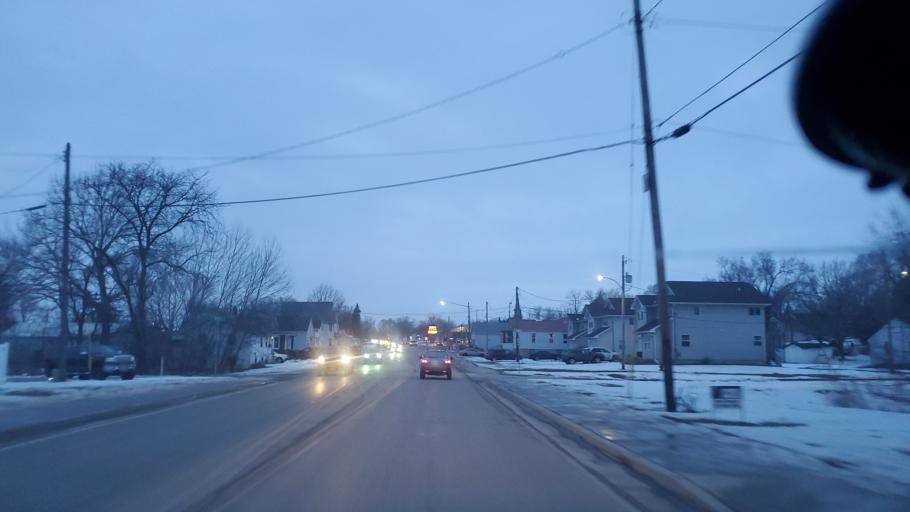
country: US
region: Illinois
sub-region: LaSalle County
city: La Salle
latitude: 41.3333
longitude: -89.0845
